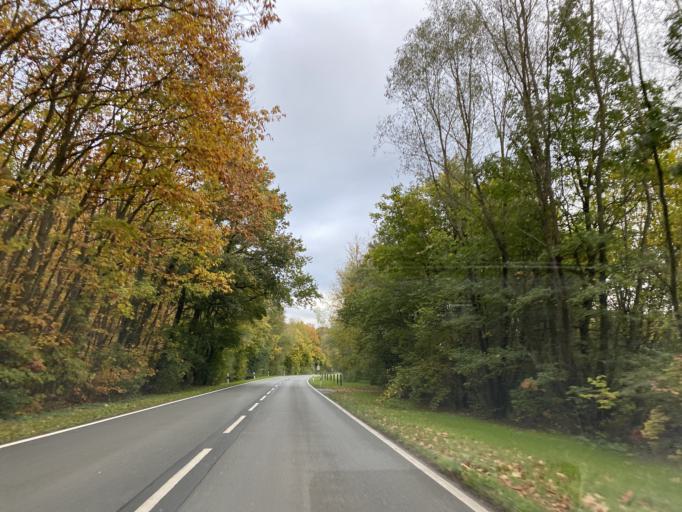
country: DE
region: Hesse
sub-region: Regierungsbezirk Darmstadt
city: Buttelborn
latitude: 49.9446
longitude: 8.5432
